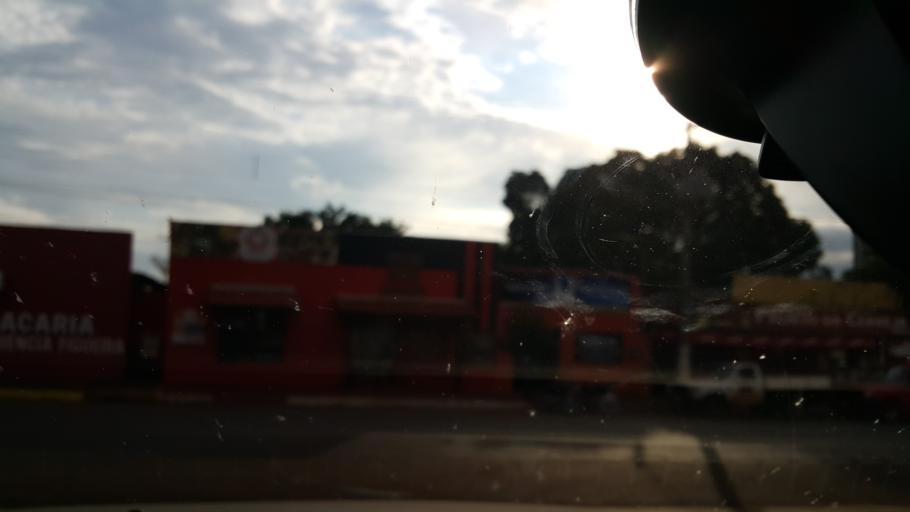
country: BR
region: Mato Grosso do Sul
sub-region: Maracaju
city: Maracaju
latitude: -21.6300
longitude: -55.1595
